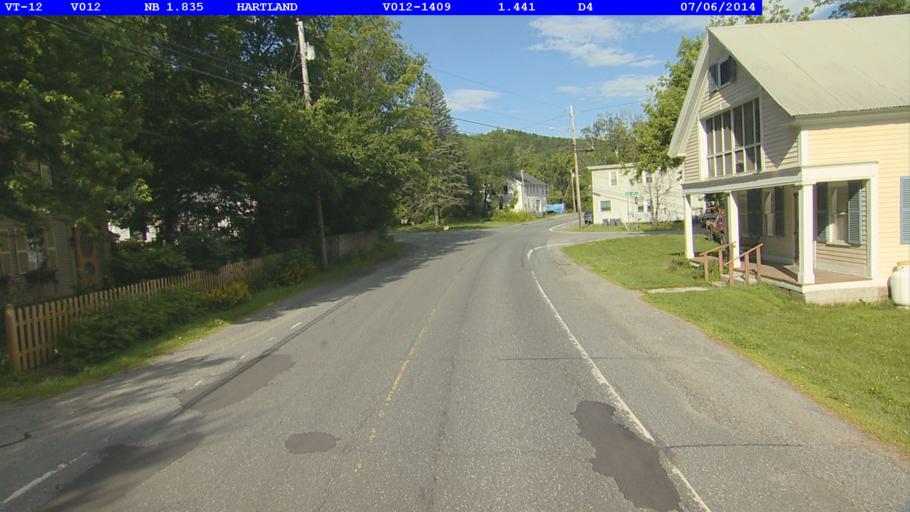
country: US
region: Vermont
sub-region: Windsor County
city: Windsor
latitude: 43.5465
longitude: -72.4246
